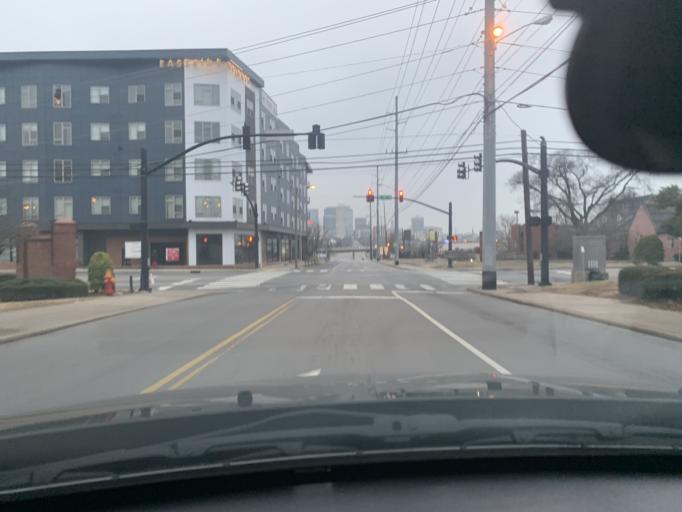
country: US
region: Tennessee
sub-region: Davidson County
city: Nashville
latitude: 36.1720
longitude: -86.7644
